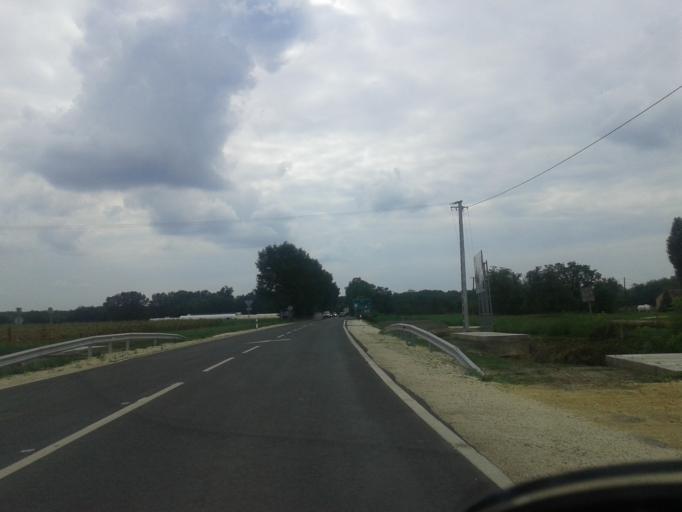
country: HU
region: Csongrad
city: Morahalom
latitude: 46.2265
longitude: 19.8333
